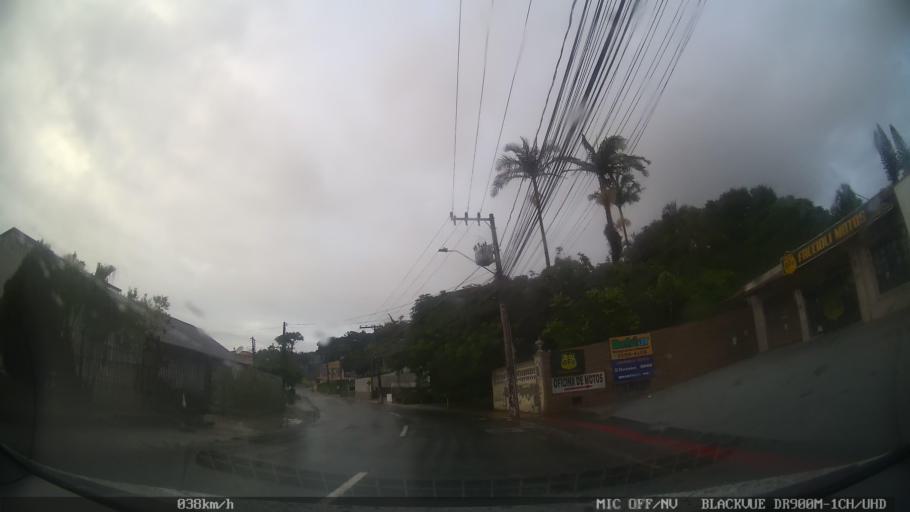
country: BR
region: Santa Catarina
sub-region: Sao Jose
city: Campinas
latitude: -27.6102
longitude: -48.6283
